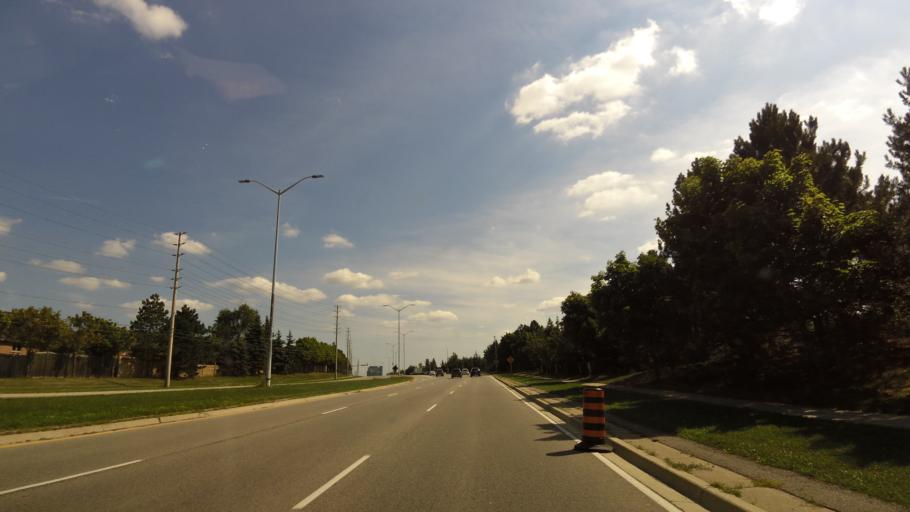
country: CA
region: Ontario
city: Mississauga
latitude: 43.5750
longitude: -79.7295
